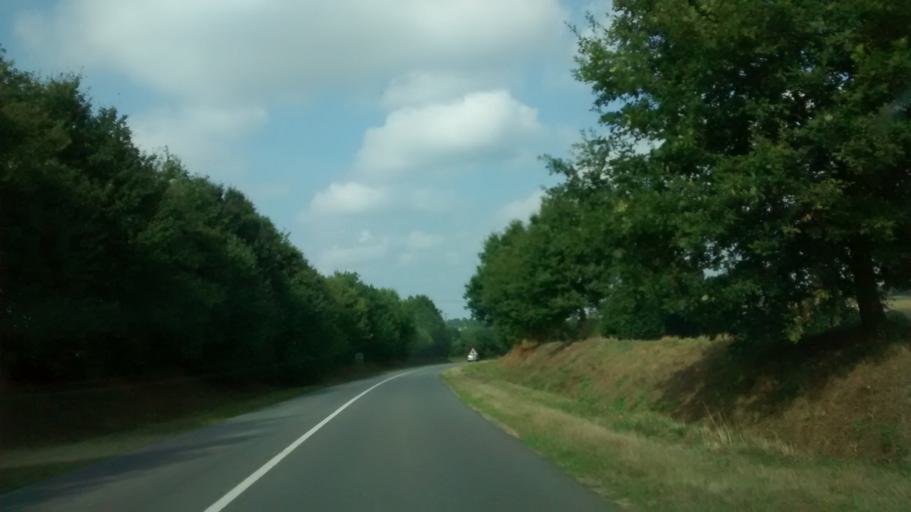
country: FR
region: Brittany
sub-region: Departement d'Ille-et-Vilaine
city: Livre-sur-Changeon
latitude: 48.2243
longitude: -1.3501
